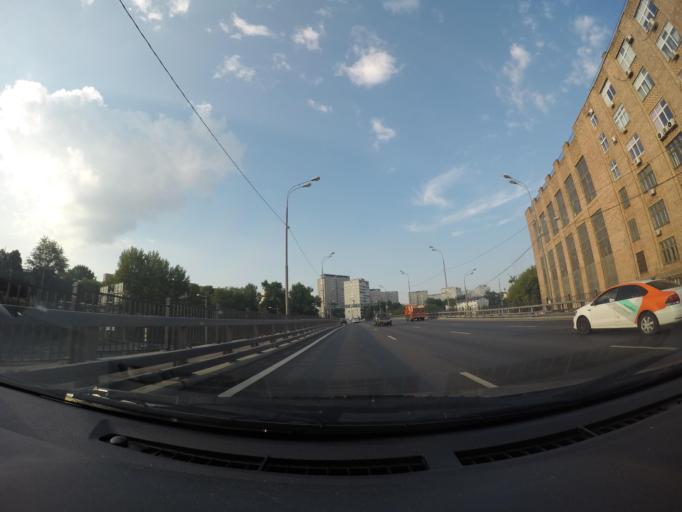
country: RU
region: Moscow
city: Lefortovo
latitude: 55.7617
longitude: 37.6848
